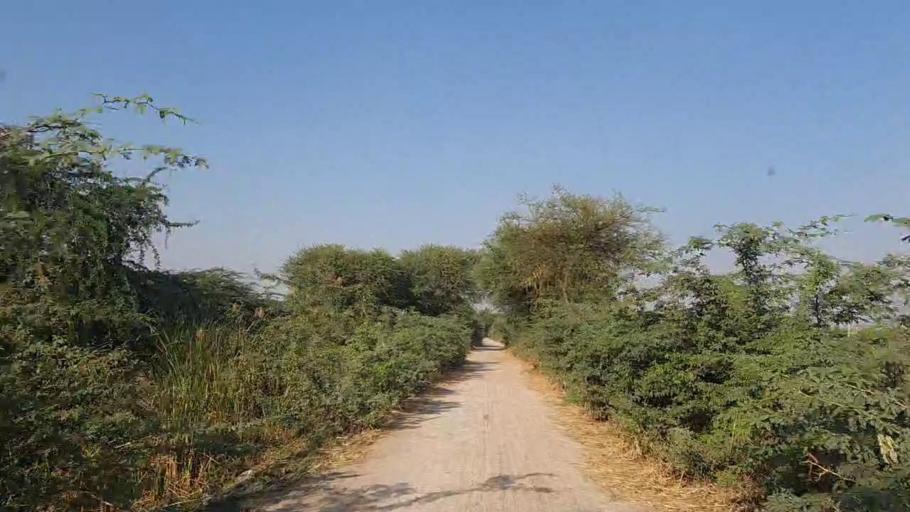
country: PK
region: Sindh
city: Thatta
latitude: 24.7654
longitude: 67.9656
